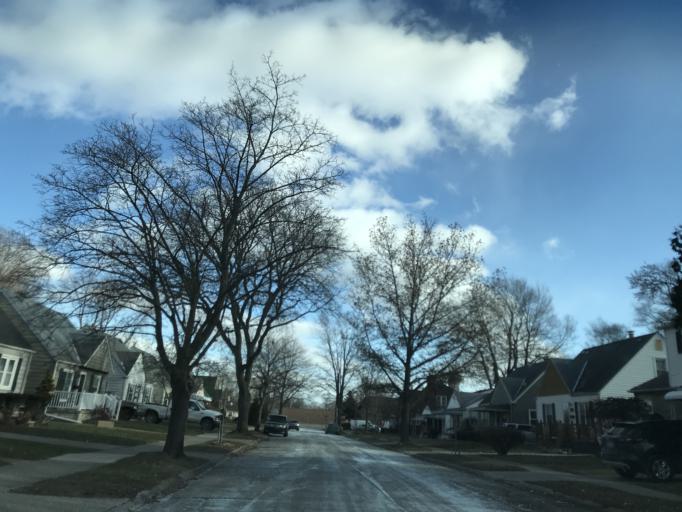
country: US
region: Michigan
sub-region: Oakland County
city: Madison Heights
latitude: 42.4803
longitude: -83.1153
